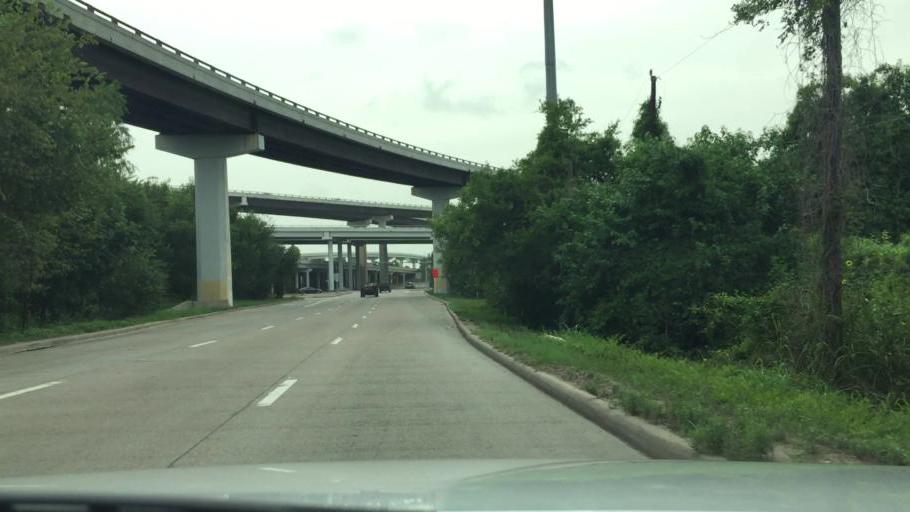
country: US
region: Texas
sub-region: Harris County
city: Cloverleaf
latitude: 29.7722
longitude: -95.1513
